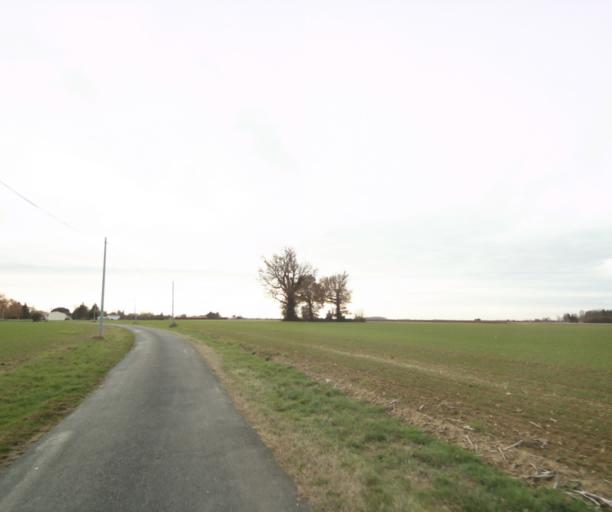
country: FR
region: Poitou-Charentes
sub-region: Departement de la Charente-Maritime
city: Corme-Royal
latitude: 45.7545
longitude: -0.8092
